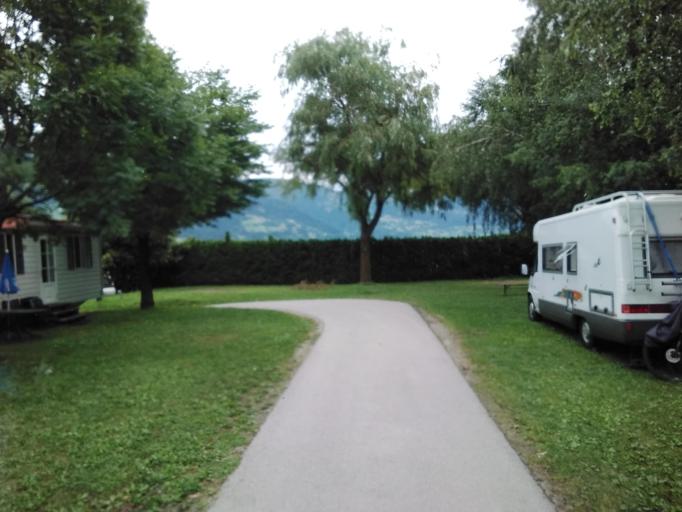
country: AT
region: Tyrol
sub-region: Politischer Bezirk Lienz
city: Amlach
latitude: 46.8126
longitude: 12.7645
